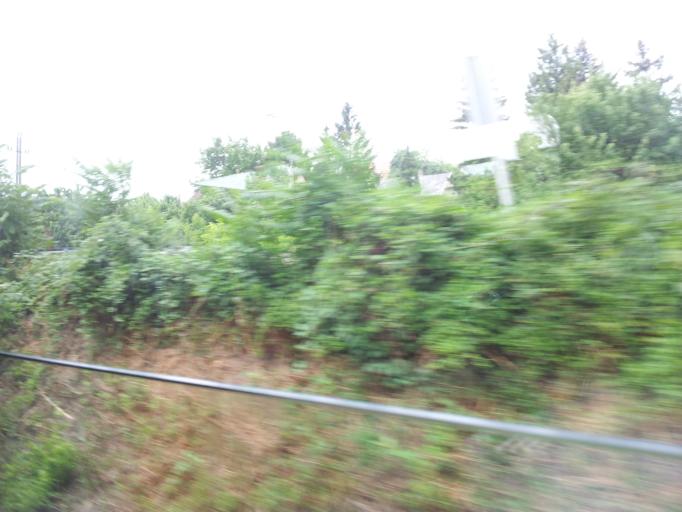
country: HU
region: Veszprem
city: Zanka
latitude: 46.8598
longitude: 17.6711
